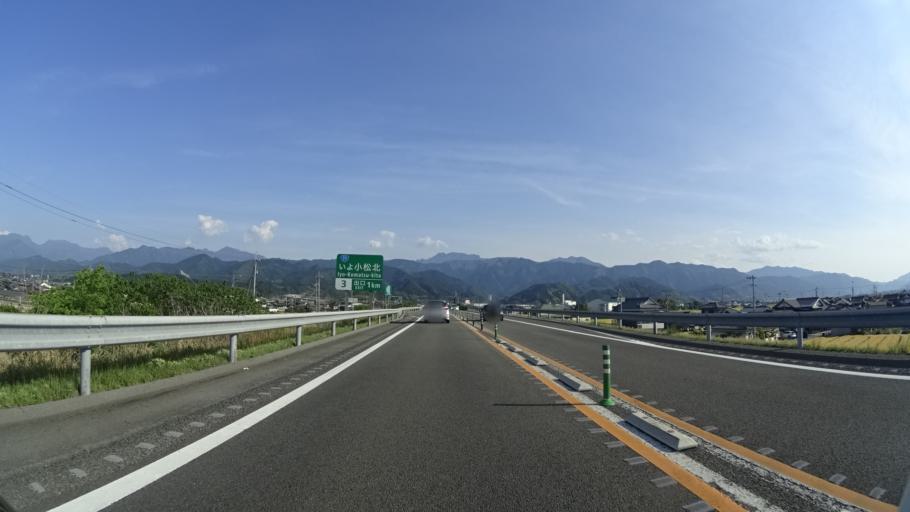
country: JP
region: Ehime
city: Saijo
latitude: 33.9027
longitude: 133.0756
